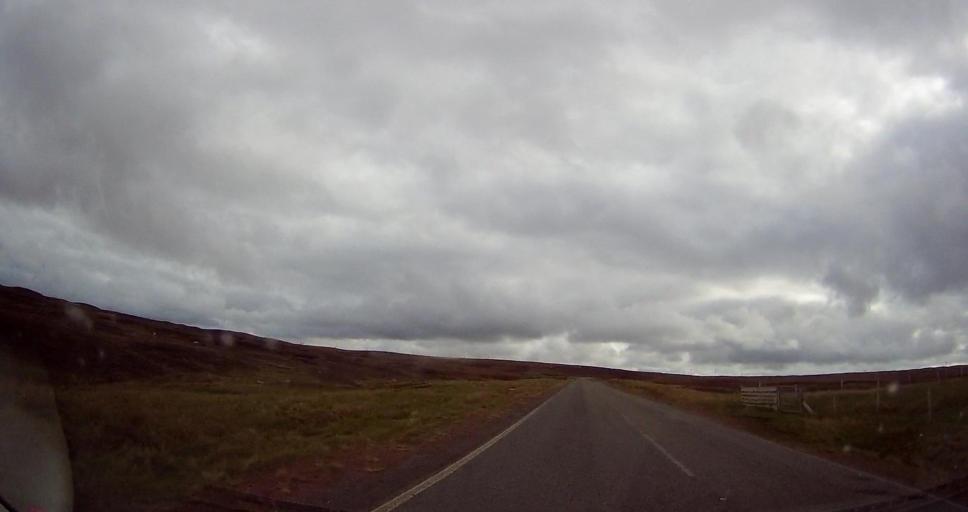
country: GB
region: Scotland
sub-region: Shetland Islands
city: Shetland
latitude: 60.6627
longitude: -1.0421
